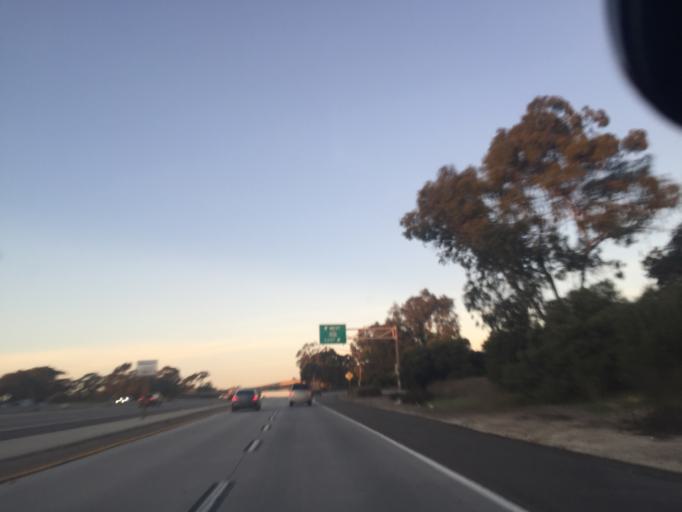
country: MX
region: Baja California
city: Tijuana
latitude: 32.5635
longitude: -117.0413
